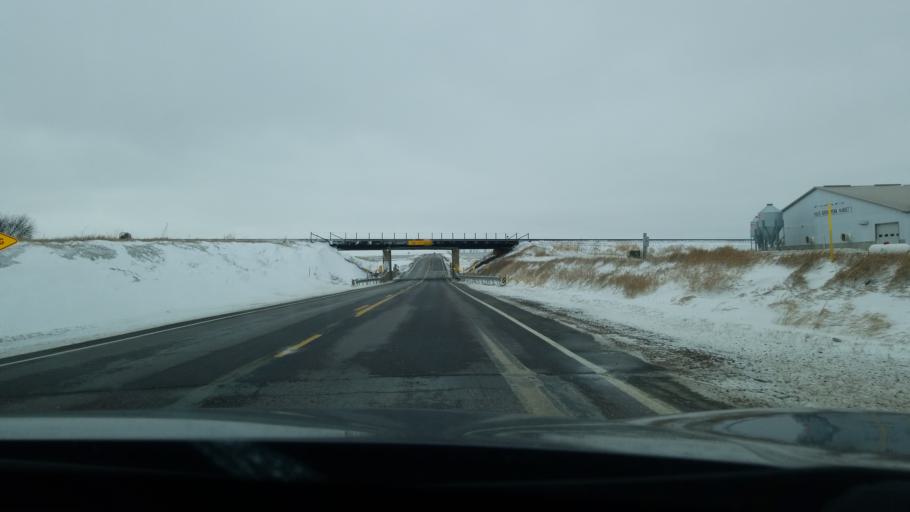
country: US
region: Iowa
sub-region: Sioux County
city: Hull
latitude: 43.2195
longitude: -96.1773
